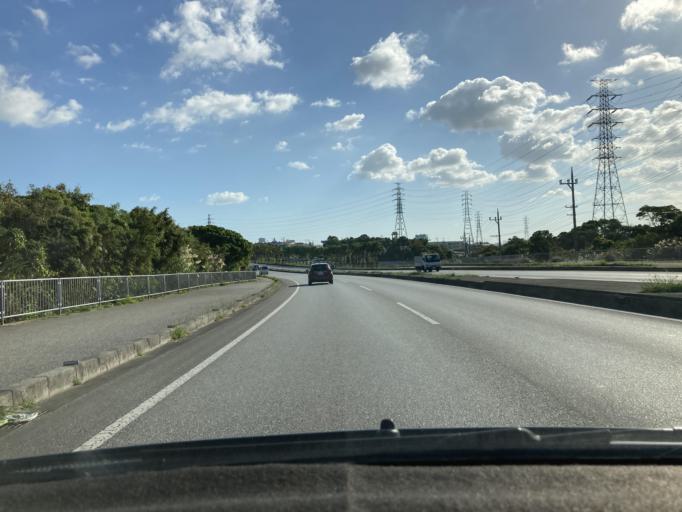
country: JP
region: Okinawa
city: Ishikawa
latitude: 26.3908
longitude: 127.8279
